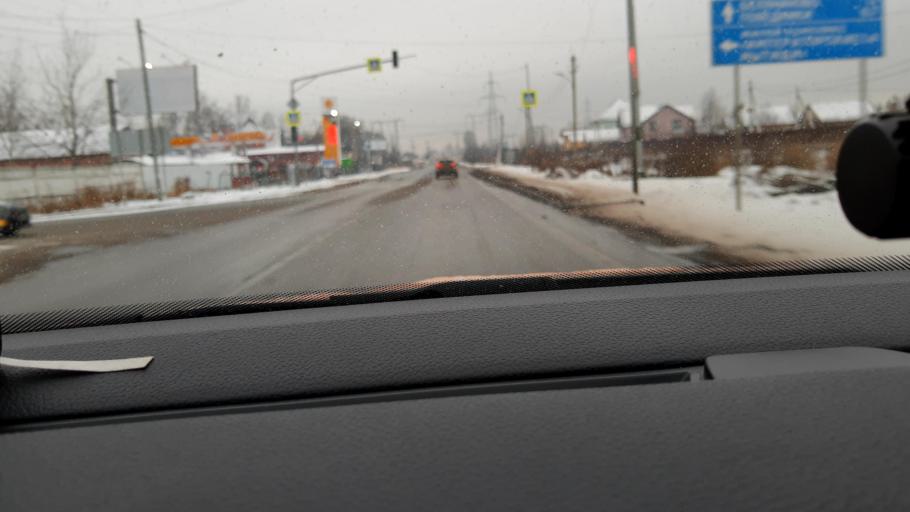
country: RU
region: Moskovskaya
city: Povedniki
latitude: 55.9611
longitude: 37.6617
